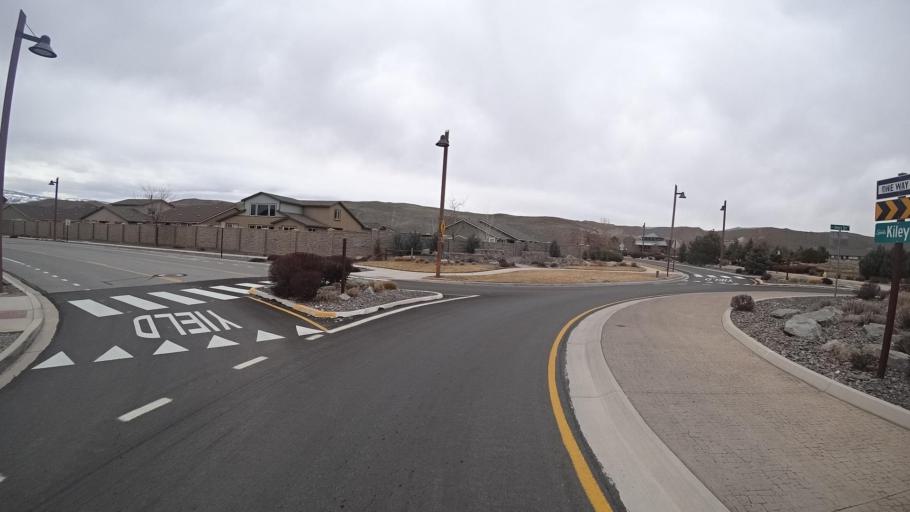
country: US
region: Nevada
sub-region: Washoe County
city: Spanish Springs
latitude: 39.6037
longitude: -119.7252
